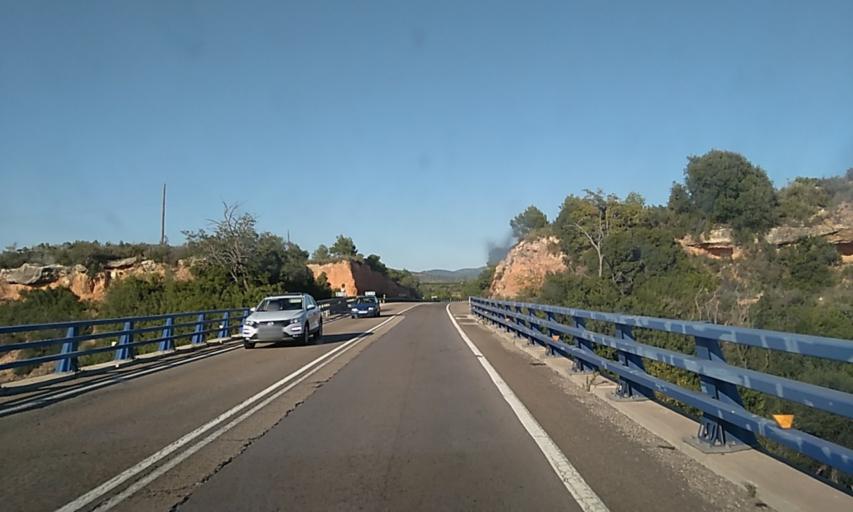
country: ES
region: Valencia
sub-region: Provincia de Castello
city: Torreblanca
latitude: 40.2372
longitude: 0.2238
